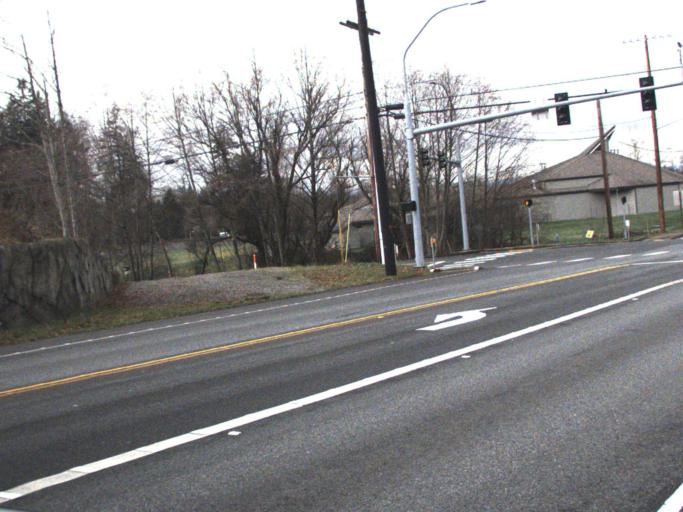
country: US
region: Washington
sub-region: Snohomish County
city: Marysville
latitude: 48.0535
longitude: -122.1187
